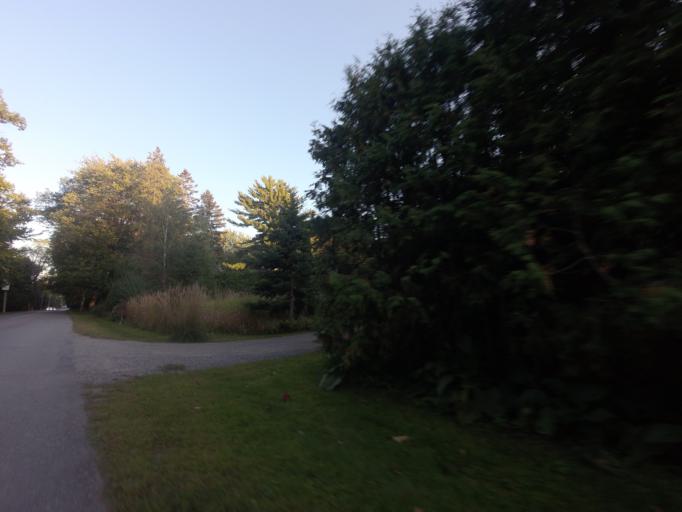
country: CA
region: Quebec
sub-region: Monteregie
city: Hudson
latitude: 45.4670
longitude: -74.1588
